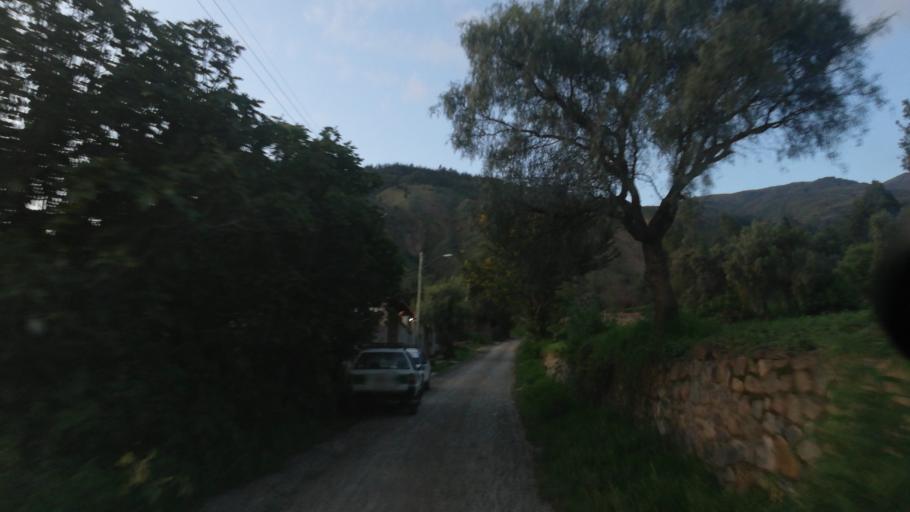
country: BO
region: Cochabamba
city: Cochabamba
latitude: -17.3194
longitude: -66.2081
